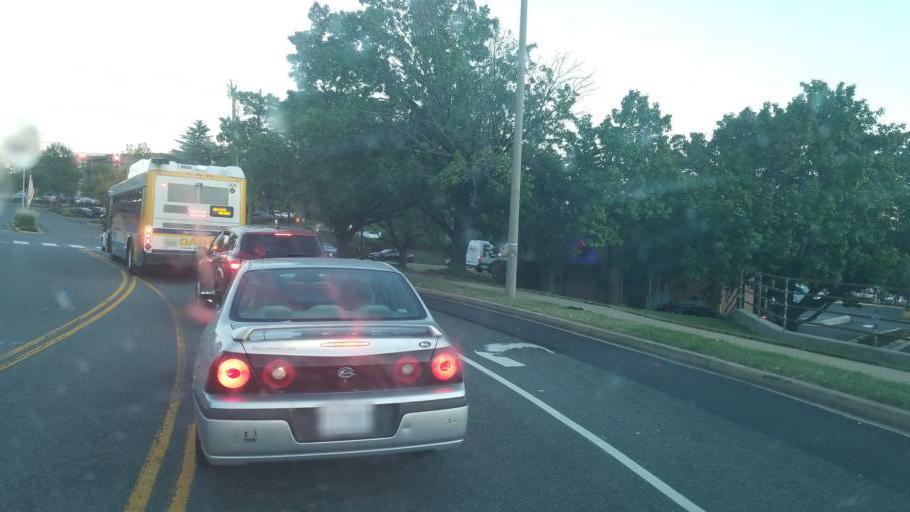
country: US
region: Virginia
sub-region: Fairfax County
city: Lincolnia
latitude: 38.8115
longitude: -77.1325
